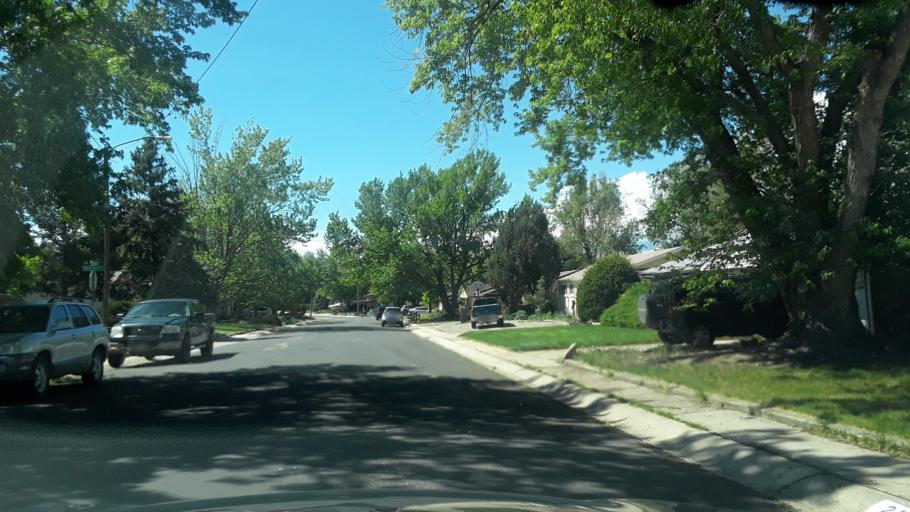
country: US
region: Colorado
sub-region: El Paso County
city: Colorado Springs
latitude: 38.8961
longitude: -104.8169
